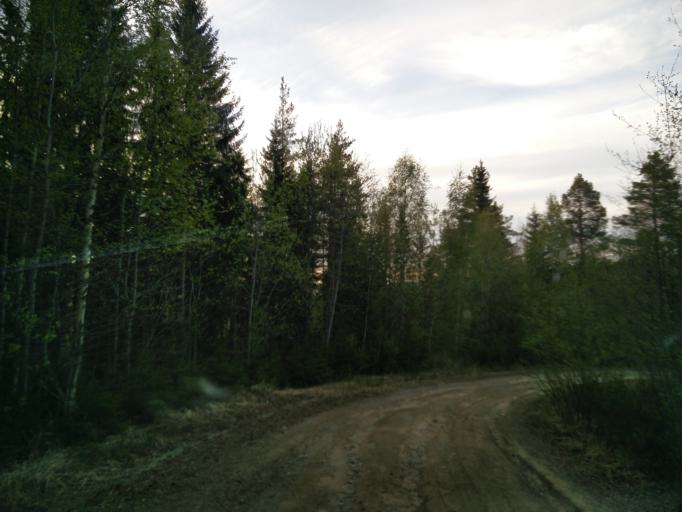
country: SE
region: Vaesternorrland
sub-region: Sundsvalls Kommun
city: Matfors
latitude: 62.3990
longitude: 16.8151
